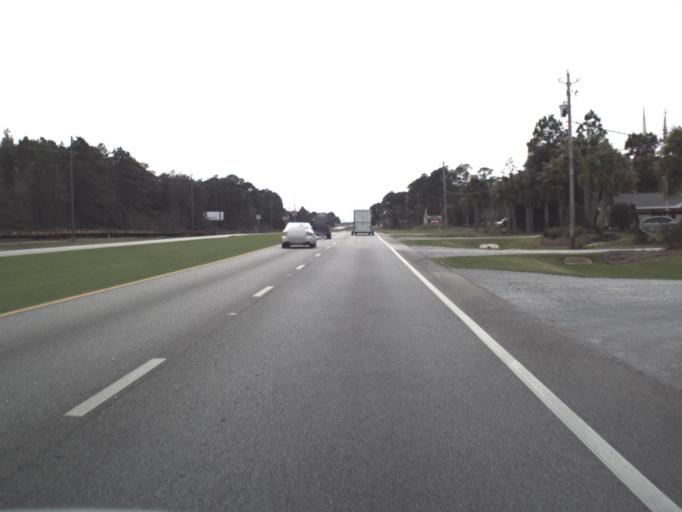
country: US
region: Florida
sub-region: Bay County
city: Hiland Park
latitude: 30.2092
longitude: -85.6133
